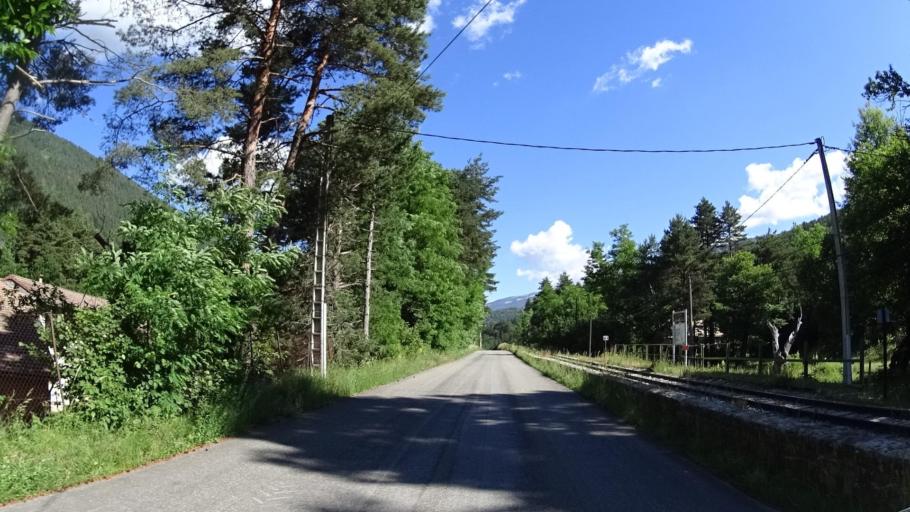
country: FR
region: Provence-Alpes-Cote d'Azur
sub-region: Departement des Alpes-de-Haute-Provence
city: Annot
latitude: 43.9858
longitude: 6.6482
